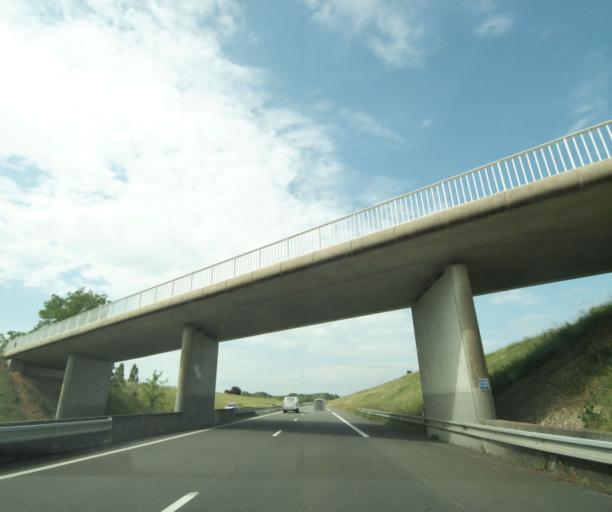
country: FR
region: Pays de la Loire
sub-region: Departement de Maine-et-Loire
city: Saint-Philbert-du-Peuple
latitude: 47.3708
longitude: -0.0840
